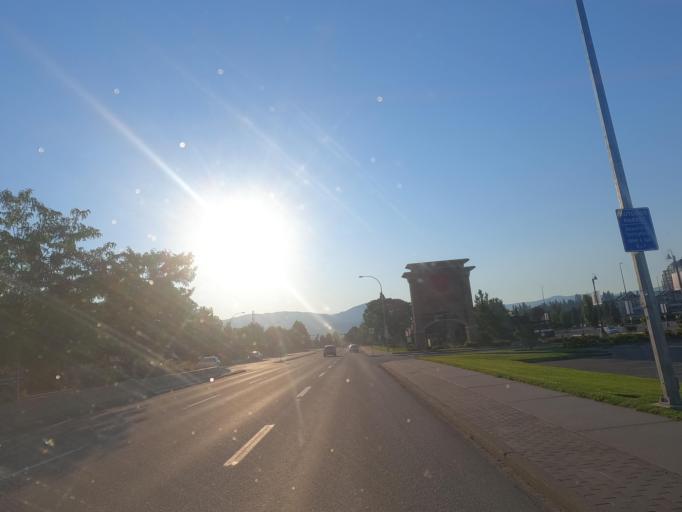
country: CA
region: British Columbia
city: Kelowna
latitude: 49.8816
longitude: -119.4412
